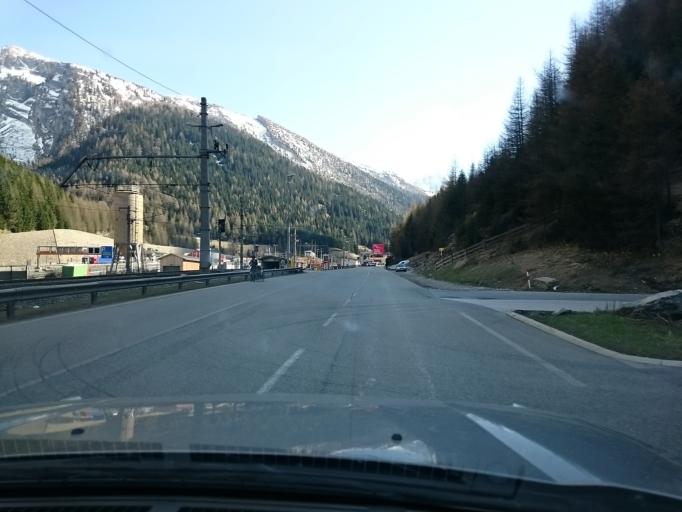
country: AT
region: Tyrol
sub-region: Politischer Bezirk Innsbruck Land
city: Gries am Brenner
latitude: 47.0117
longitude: 11.5070
